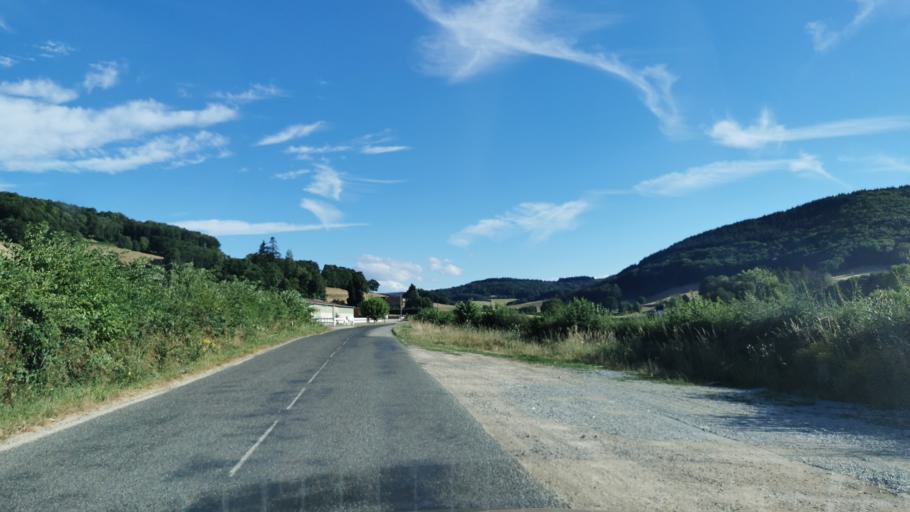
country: FR
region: Bourgogne
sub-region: Departement de Saone-et-Loire
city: Marmagne
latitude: 46.8419
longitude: 4.3191
